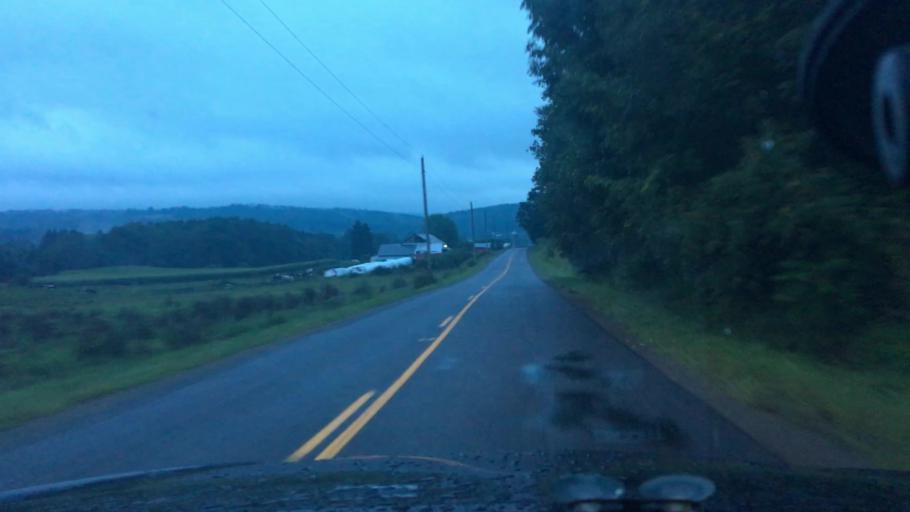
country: US
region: New York
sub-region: Cattaraugus County
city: Little Valley
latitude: 42.2432
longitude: -78.8899
